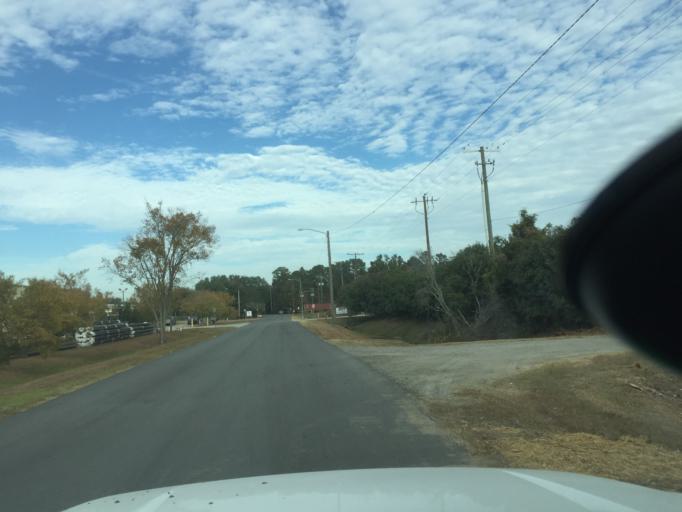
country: US
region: Georgia
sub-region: Chatham County
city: Garden City
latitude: 32.0815
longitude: -81.1458
